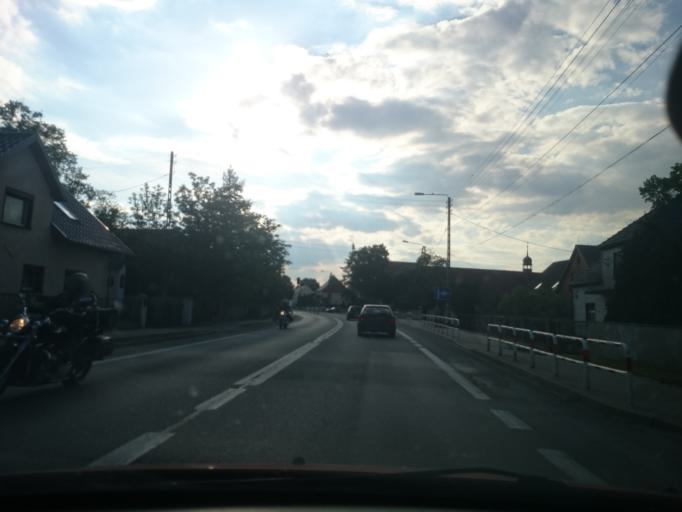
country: PL
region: Opole Voivodeship
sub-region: Powiat opolski
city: Naklo
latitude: 50.5792
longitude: 18.1213
